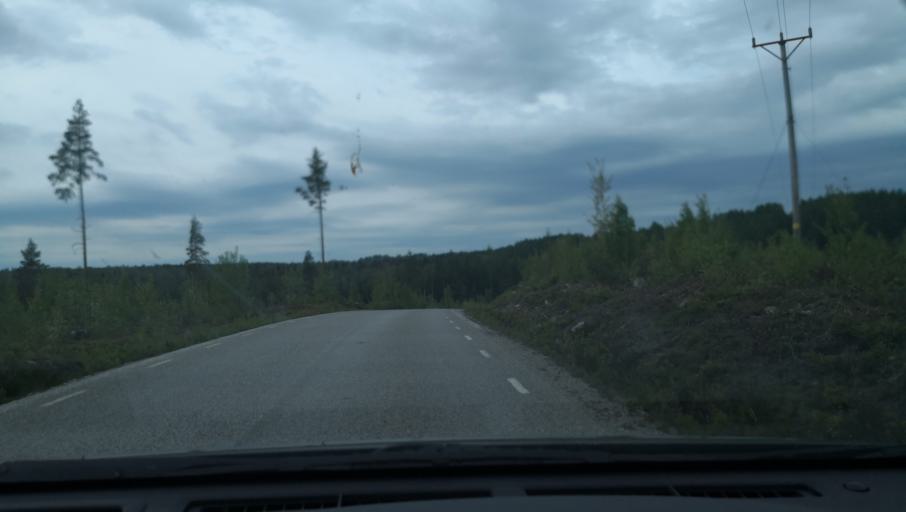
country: SE
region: Vaestmanland
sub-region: Skinnskattebergs Kommun
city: Skinnskatteberg
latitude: 59.8291
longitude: 15.5775
